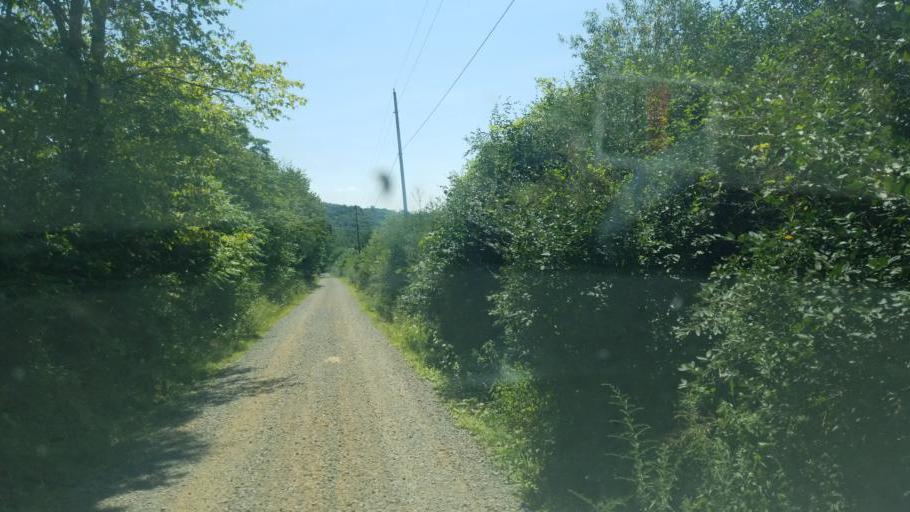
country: US
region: Pennsylvania
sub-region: Clarion County
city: Knox
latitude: 41.1954
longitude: -79.6490
